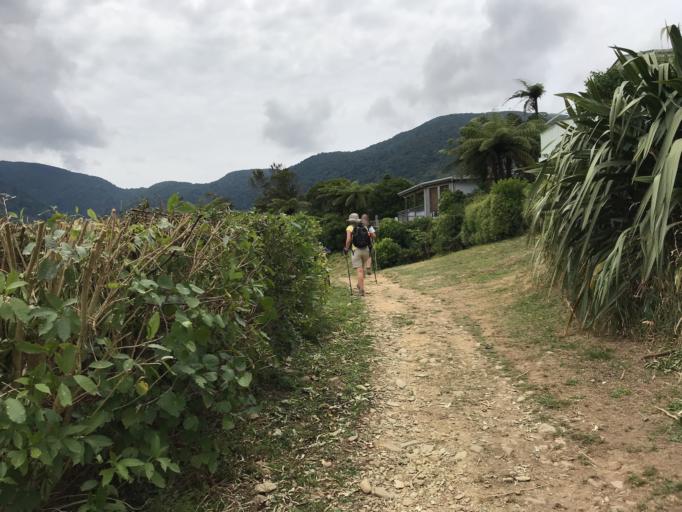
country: NZ
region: Marlborough
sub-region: Marlborough District
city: Picton
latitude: -41.1024
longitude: 174.1842
